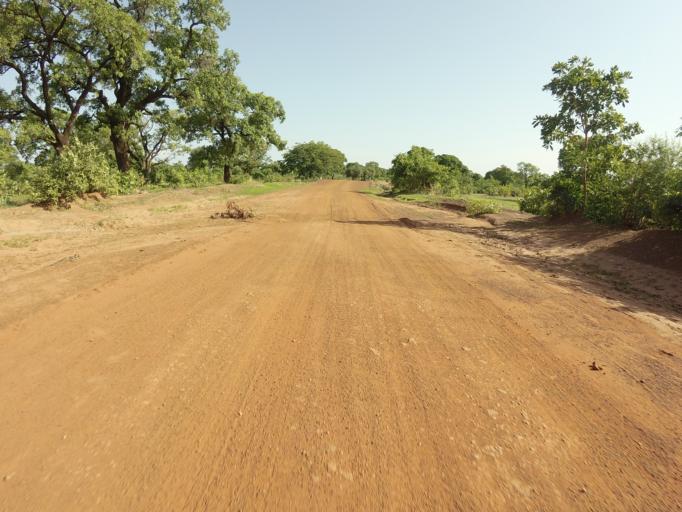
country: GH
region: Upper East
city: Bawku
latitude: 10.7396
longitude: -0.2005
